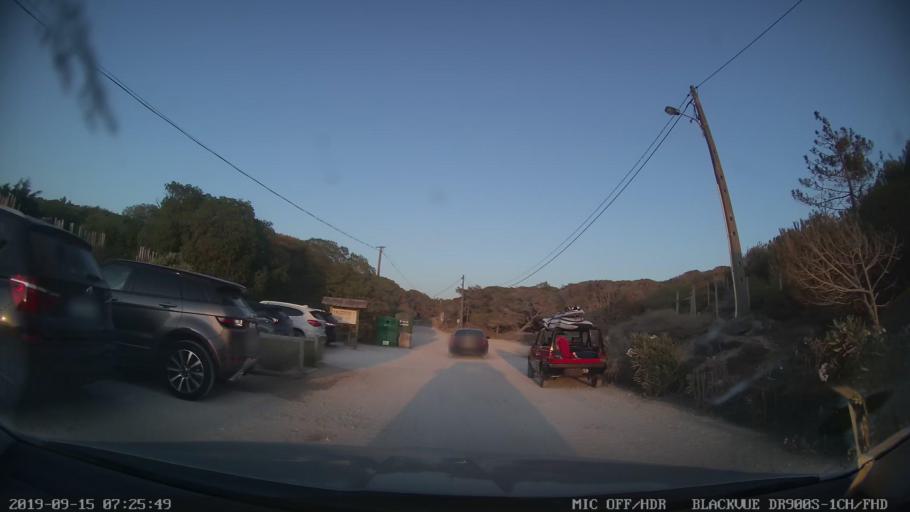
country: PT
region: Lisbon
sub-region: Cascais
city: Cascais
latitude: 38.7207
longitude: -9.4688
